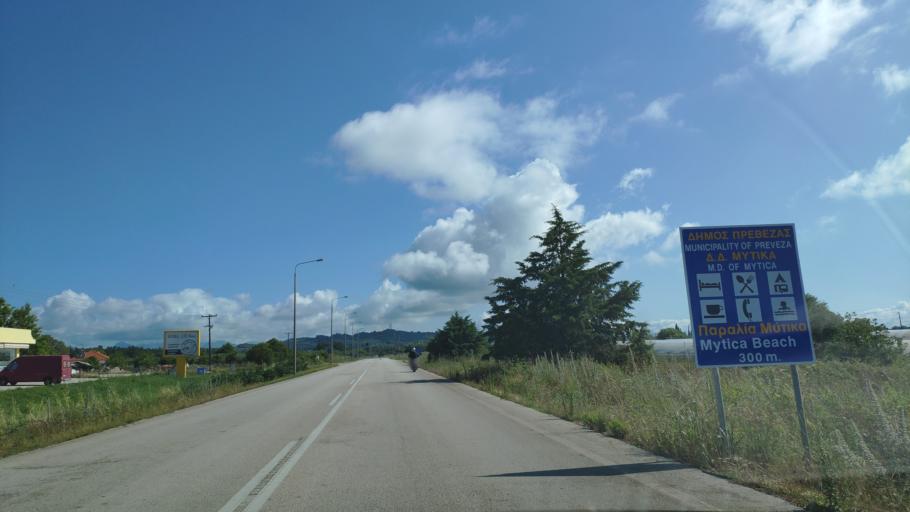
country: GR
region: Epirus
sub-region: Nomos Prevezis
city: Preveza
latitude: 38.9995
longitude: 20.7160
